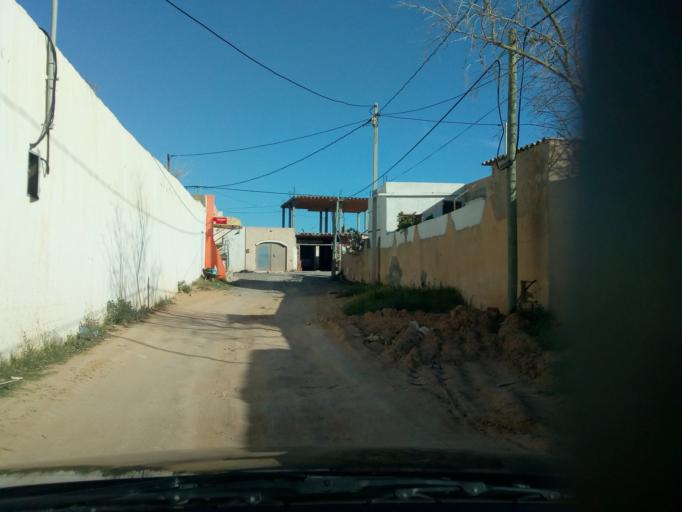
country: TN
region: Safaqis
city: Sfax
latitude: 34.7279
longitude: 10.6256
